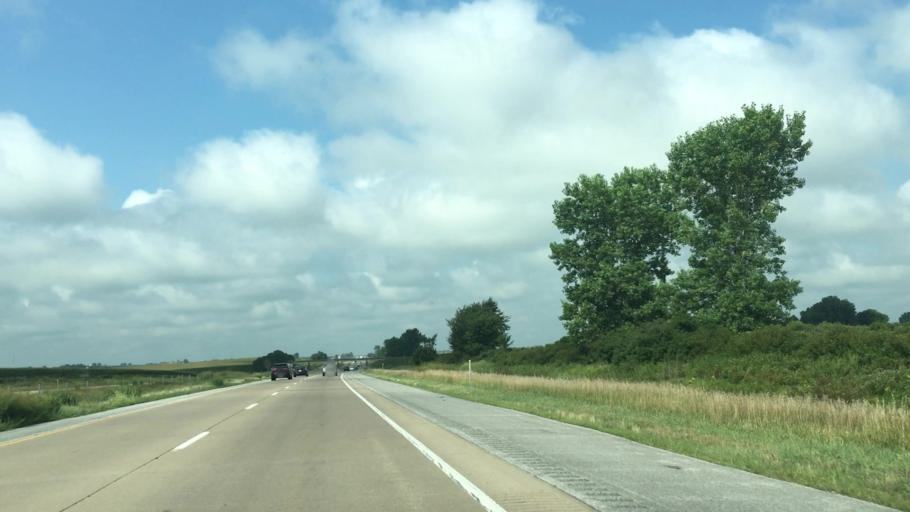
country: US
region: Iowa
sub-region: Cedar County
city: Durant
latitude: 41.6341
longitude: -90.9506
